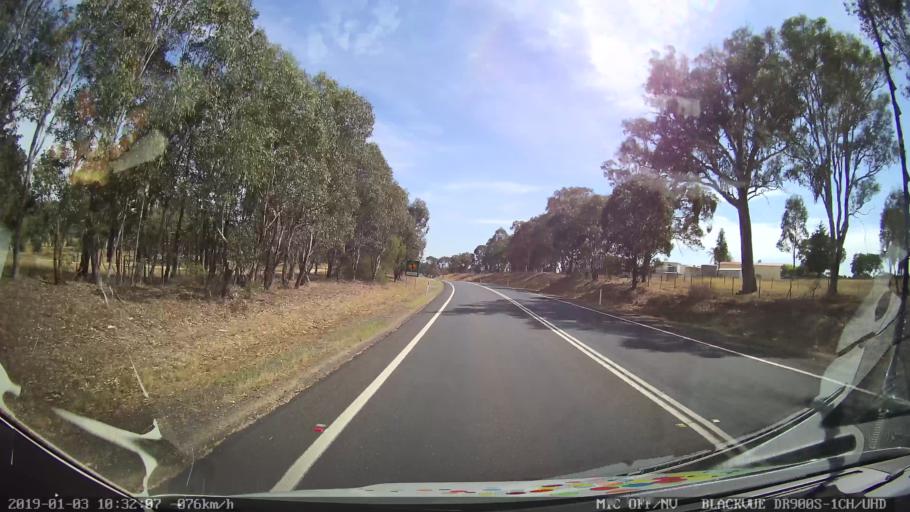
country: AU
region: New South Wales
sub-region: Young
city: Young
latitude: -34.3425
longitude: 148.2827
